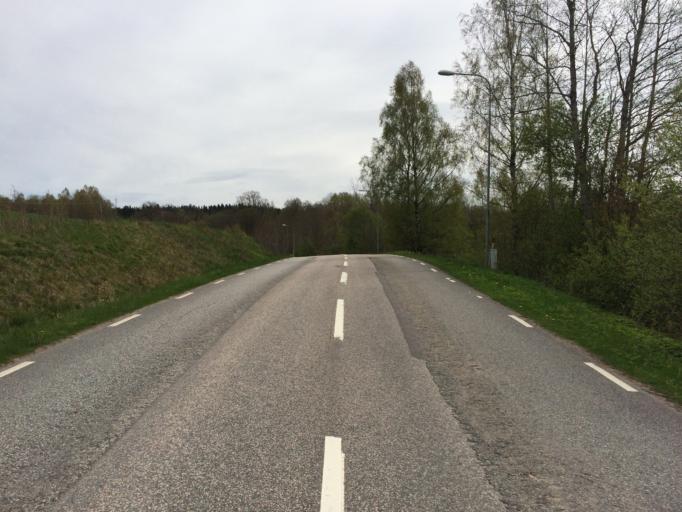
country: SE
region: Vaestra Goetaland
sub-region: Ulricehamns Kommun
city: Ulricehamn
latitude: 57.7340
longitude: 13.4281
